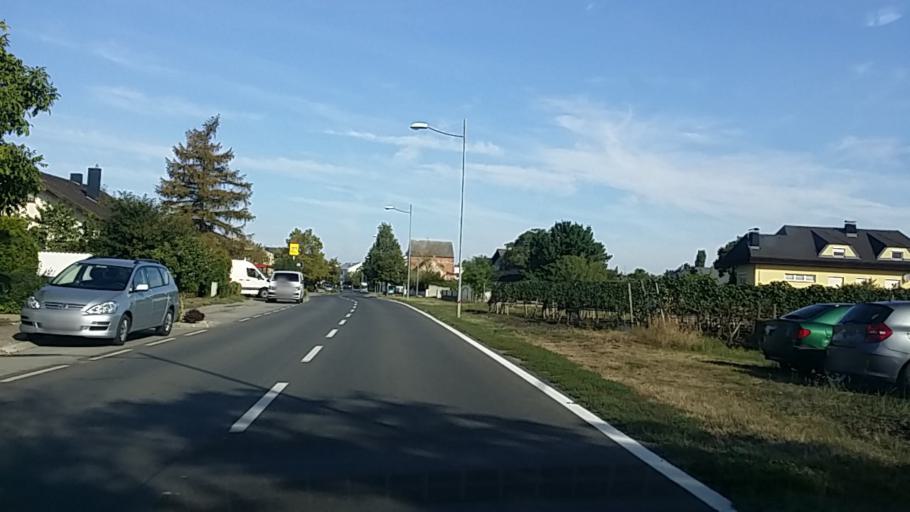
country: AT
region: Burgenland
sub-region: Politischer Bezirk Neusiedl am See
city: Illmitz
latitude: 47.7592
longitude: 16.8095
